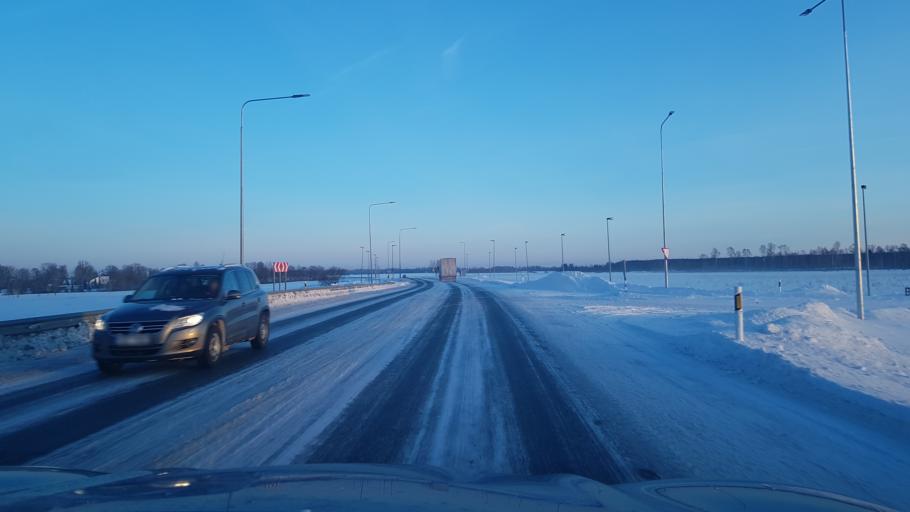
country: EE
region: Ida-Virumaa
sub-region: Narva-Joesuu linn
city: Narva-Joesuu
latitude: 59.3915
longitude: 28.0924
